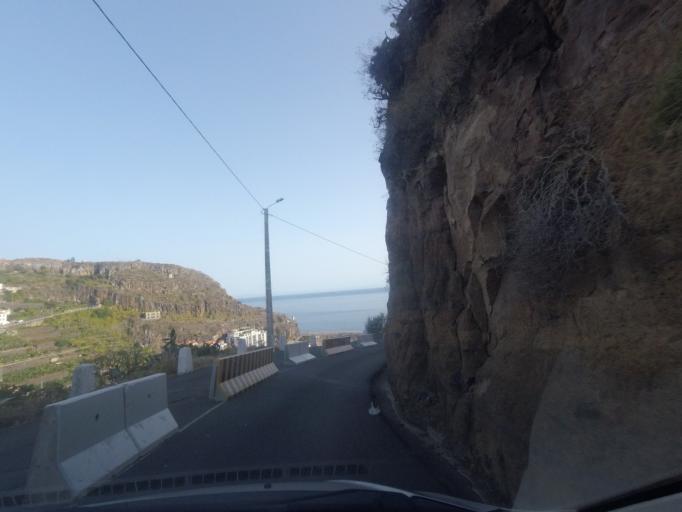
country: PT
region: Madeira
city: Ribeira Brava
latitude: 32.6732
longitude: -17.0654
